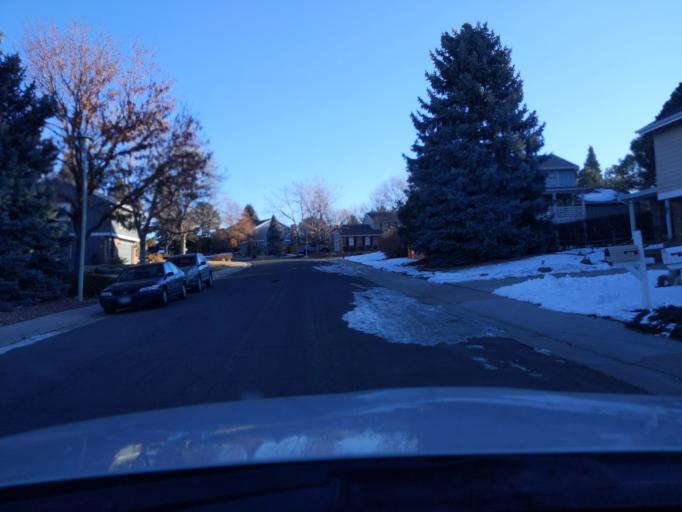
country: US
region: Colorado
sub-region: Douglas County
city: Acres Green
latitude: 39.5668
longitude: -104.8875
